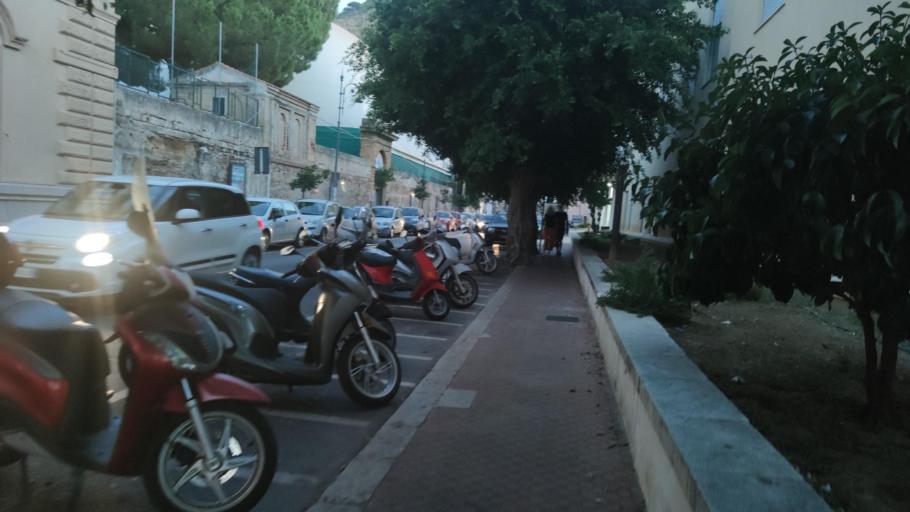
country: IT
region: Sicily
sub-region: Palermo
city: Cefalu
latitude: 38.0348
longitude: 14.0212
